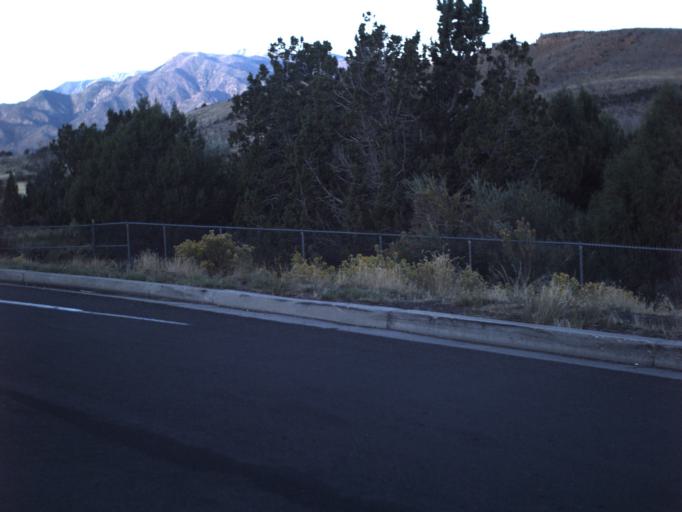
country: US
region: Utah
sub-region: Iron County
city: Cedar City
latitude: 37.5164
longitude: -113.2132
